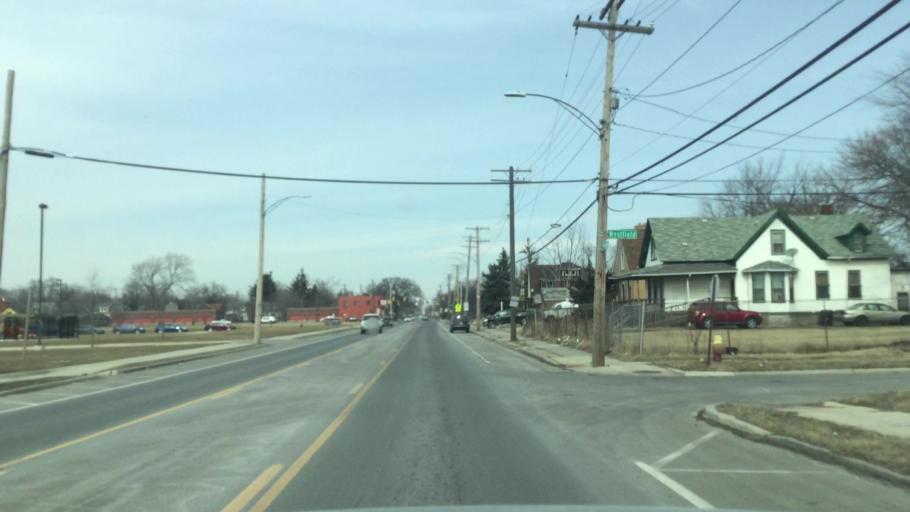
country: US
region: Michigan
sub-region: Wayne County
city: Dearborn
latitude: 42.3639
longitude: -83.1581
